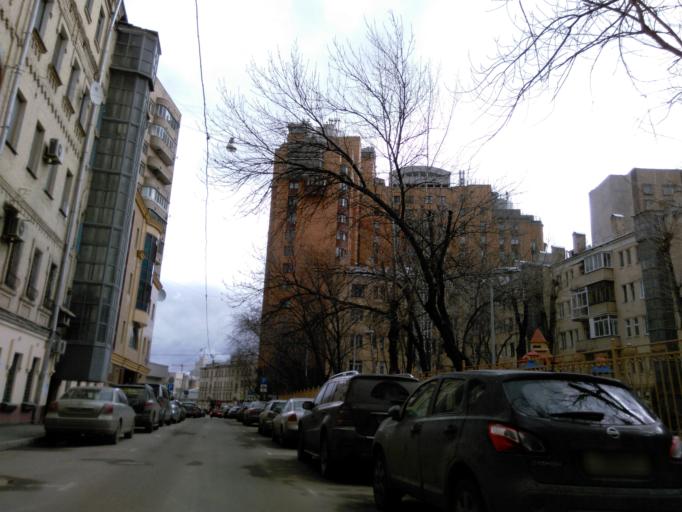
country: RU
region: Moskovskaya
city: Dorogomilovo
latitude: 55.7700
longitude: 37.5792
